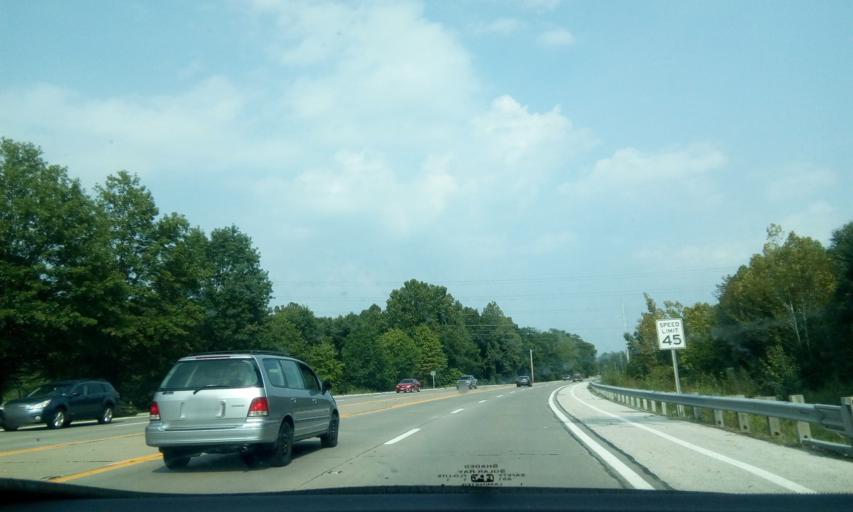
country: US
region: Missouri
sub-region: Saint Louis County
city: Town and Country
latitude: 38.5800
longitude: -90.4607
